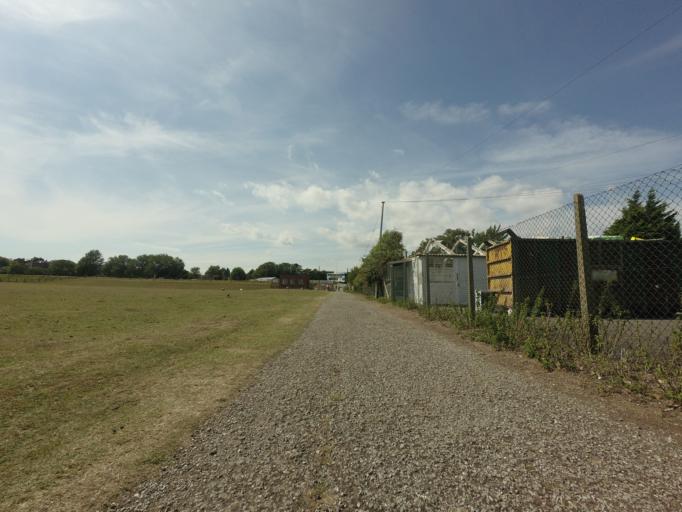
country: GB
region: England
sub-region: East Sussex
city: Rye
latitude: 50.9526
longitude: 0.7410
